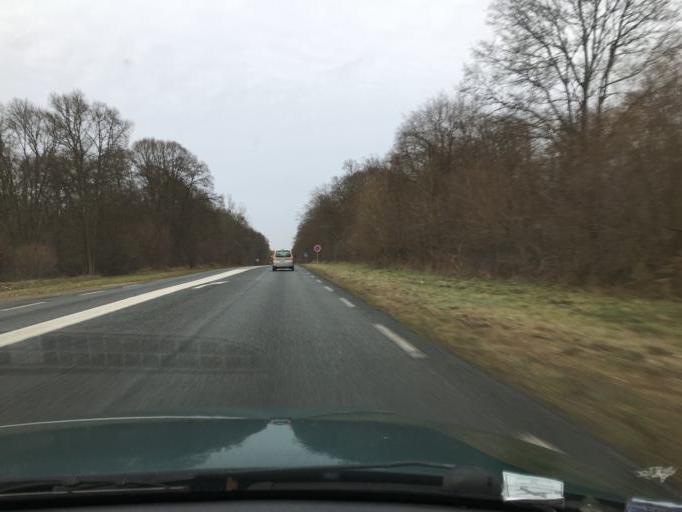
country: FR
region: Picardie
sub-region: Departement de l'Oise
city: Thiers-sur-Theve
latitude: 49.1705
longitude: 2.5598
